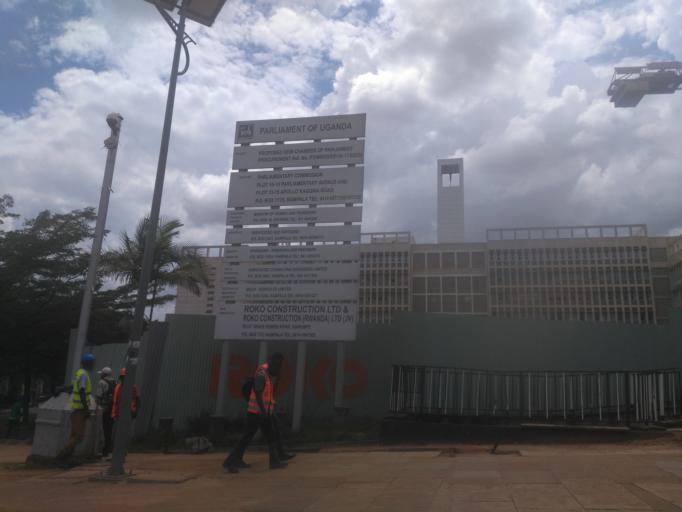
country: UG
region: Central Region
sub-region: Kampala District
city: Kampala
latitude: 0.3167
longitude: 32.5882
